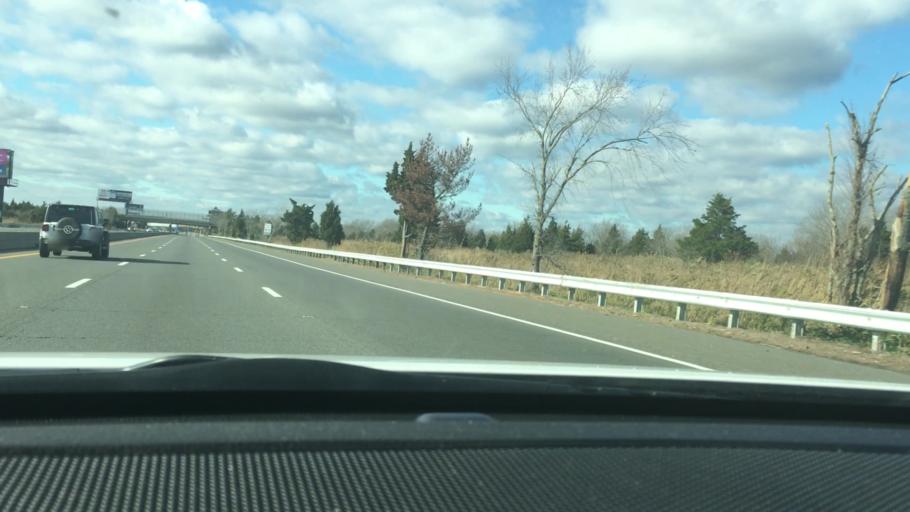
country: US
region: New Jersey
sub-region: Atlantic County
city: Ventnor City
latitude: 39.3739
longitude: -74.4745
